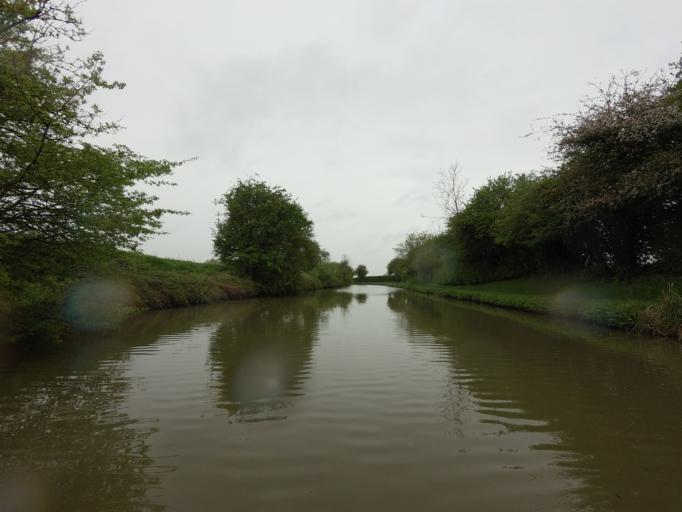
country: GB
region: England
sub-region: Milton Keynes
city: Castlethorpe
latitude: 52.0917
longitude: -0.8605
